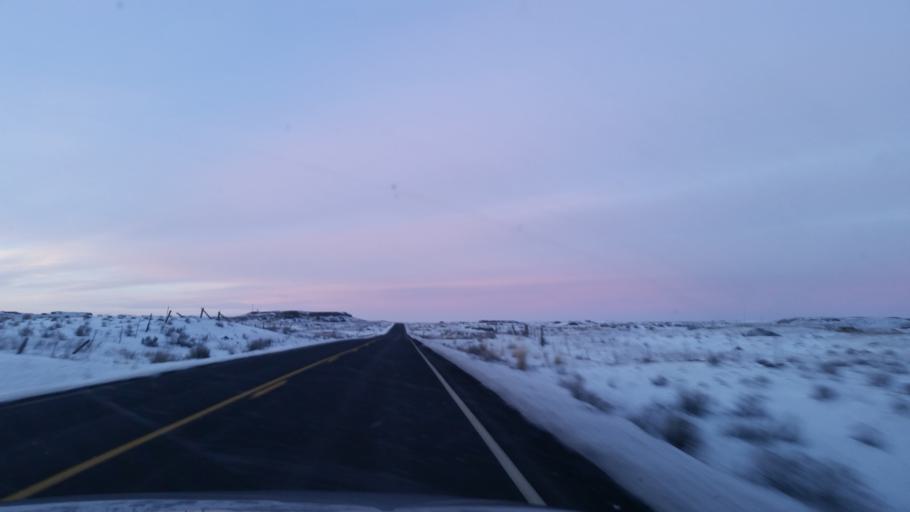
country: US
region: Washington
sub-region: Spokane County
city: Medical Lake
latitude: 47.2758
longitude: -117.9555
